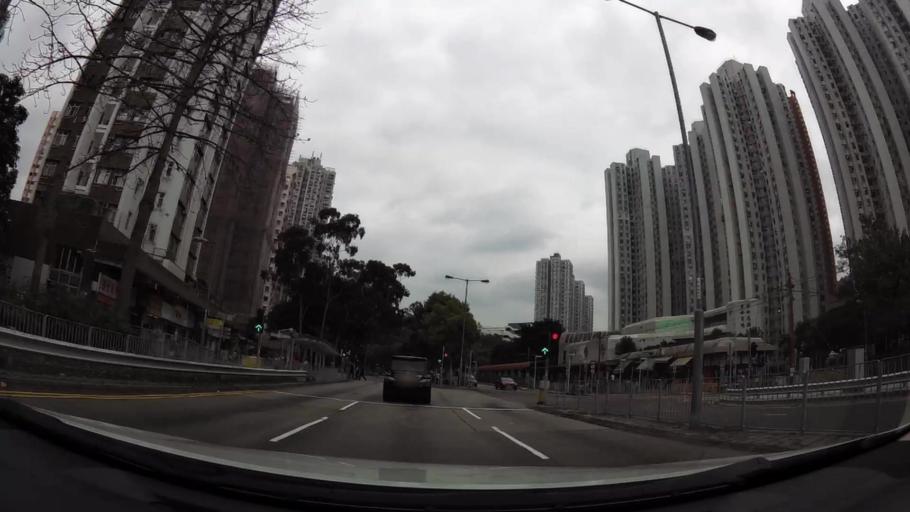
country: HK
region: Tuen Mun
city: Tuen Mun
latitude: 22.4027
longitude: 113.9790
